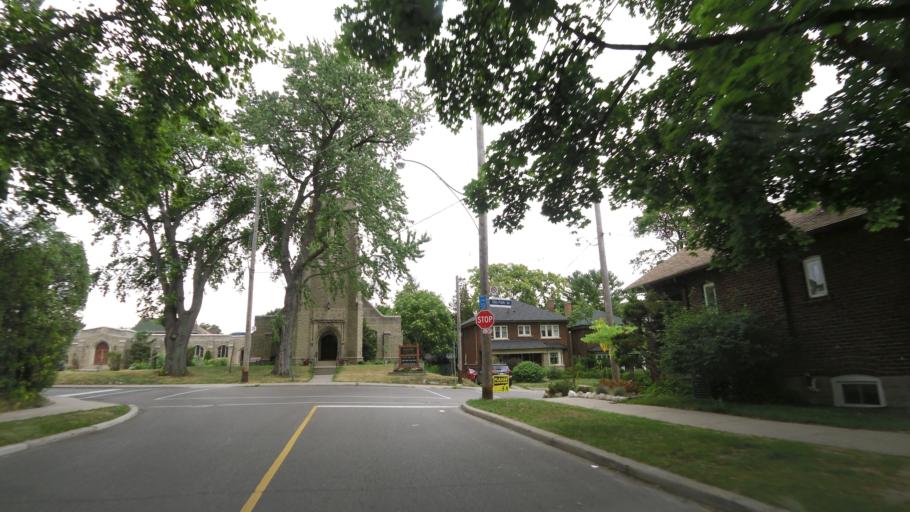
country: CA
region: Ontario
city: Toronto
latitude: 43.6460
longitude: -79.4726
